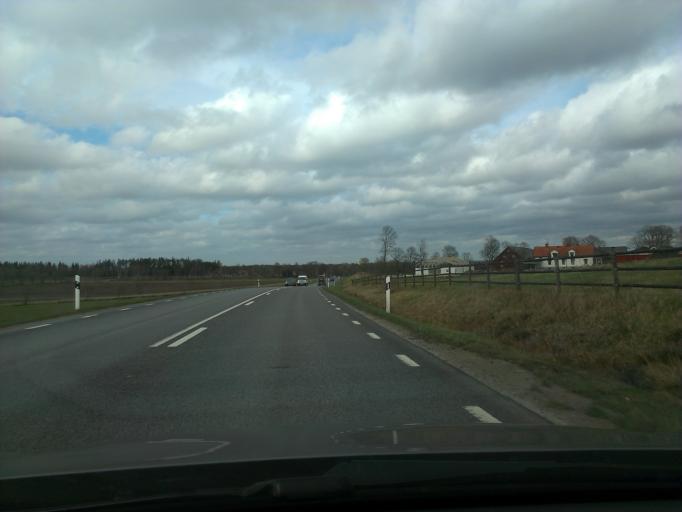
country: SE
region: Kronoberg
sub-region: Vaxjo Kommun
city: Gemla
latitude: 56.8460
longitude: 14.7153
